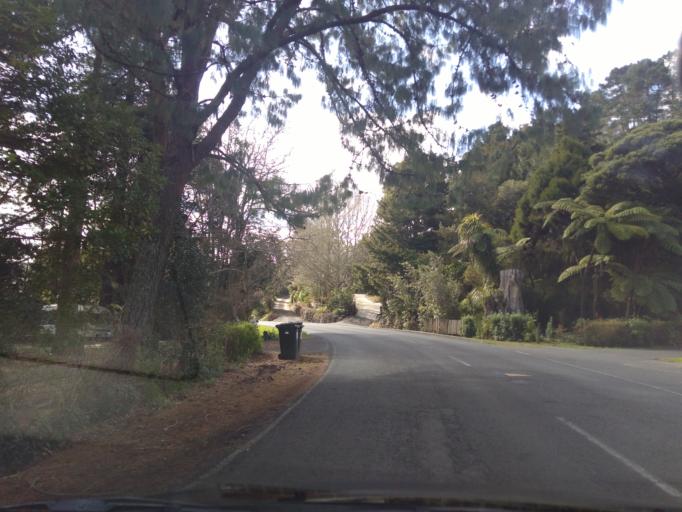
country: NZ
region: Northland
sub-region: Whangarei
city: Whangarei
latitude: -35.7017
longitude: 174.3307
